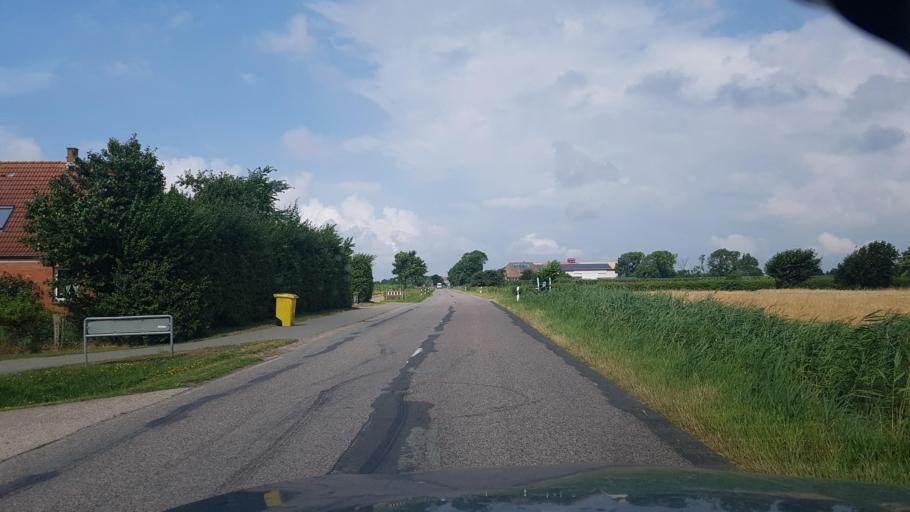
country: DE
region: Schleswig-Holstein
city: Elisabeth-Sophien-Koog
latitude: 54.4964
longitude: 8.8459
